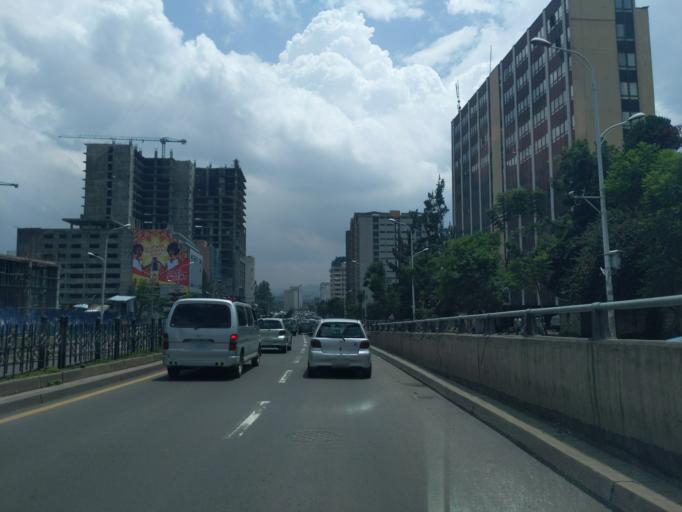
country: ET
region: Adis Abeba
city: Addis Ababa
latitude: 9.0065
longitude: 38.7670
